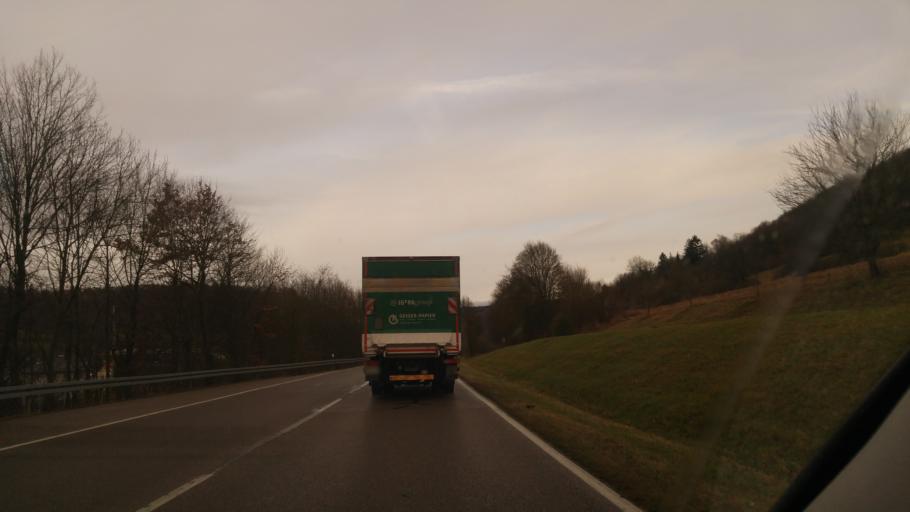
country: DE
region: Baden-Wuerttemberg
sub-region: Regierungsbezirk Stuttgart
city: Oberkochen
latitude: 48.7812
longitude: 10.1065
